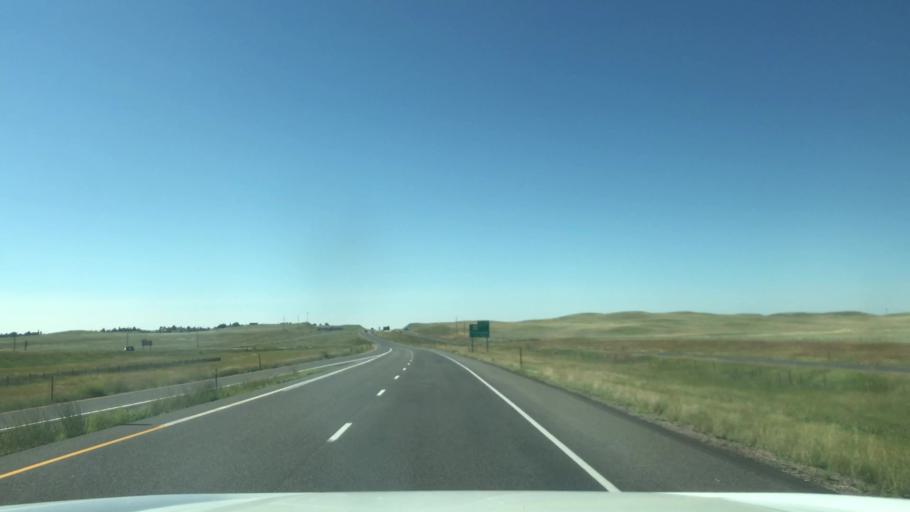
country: US
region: Wyoming
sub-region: Laramie County
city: Ranchettes
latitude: 41.2317
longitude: -104.8386
